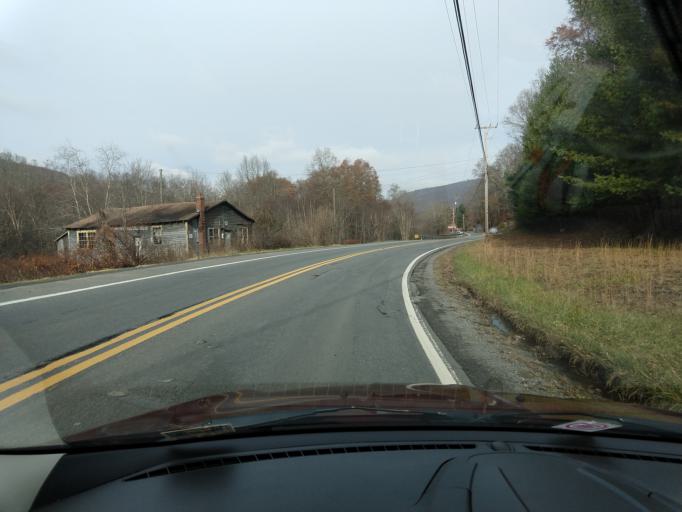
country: US
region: West Virginia
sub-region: Greenbrier County
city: Rainelle
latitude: 37.9719
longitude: -80.7077
